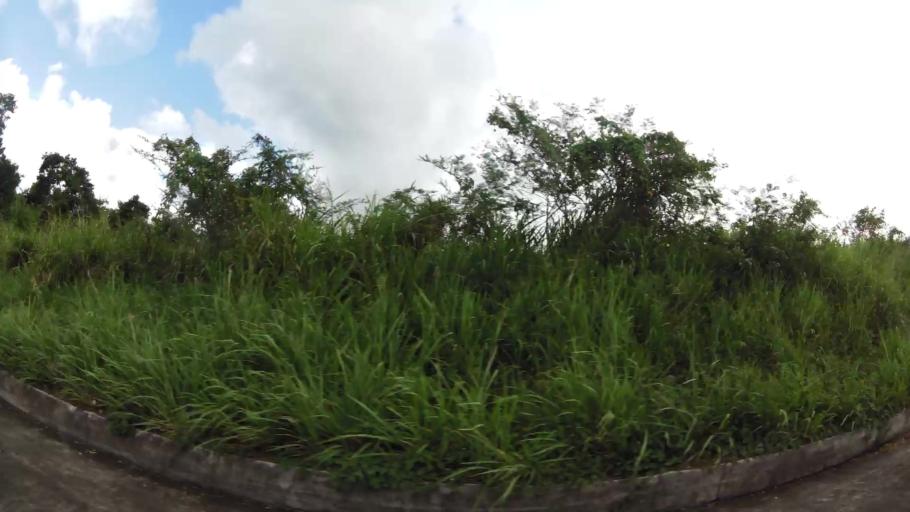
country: MQ
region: Martinique
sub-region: Martinique
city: Les Trois-Ilets
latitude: 14.5190
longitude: -60.9839
